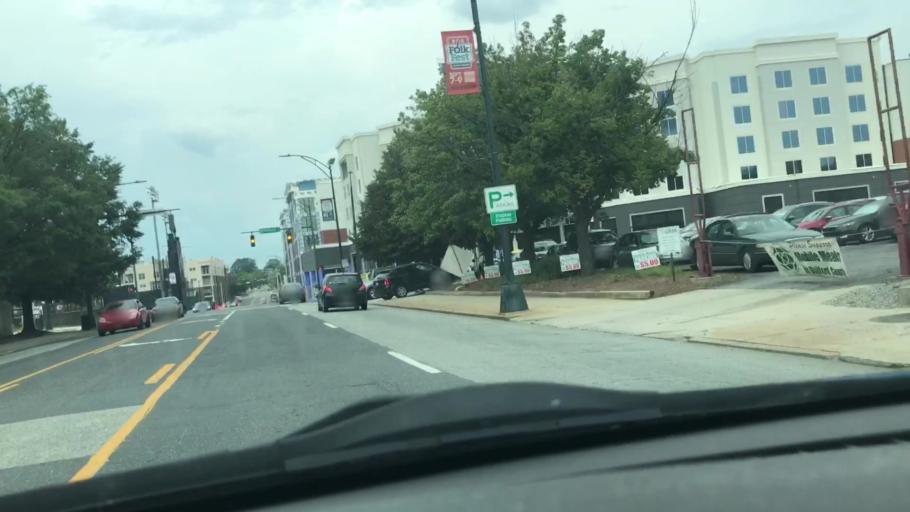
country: US
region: North Carolina
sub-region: Guilford County
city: Greensboro
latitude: 36.0739
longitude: -79.7936
